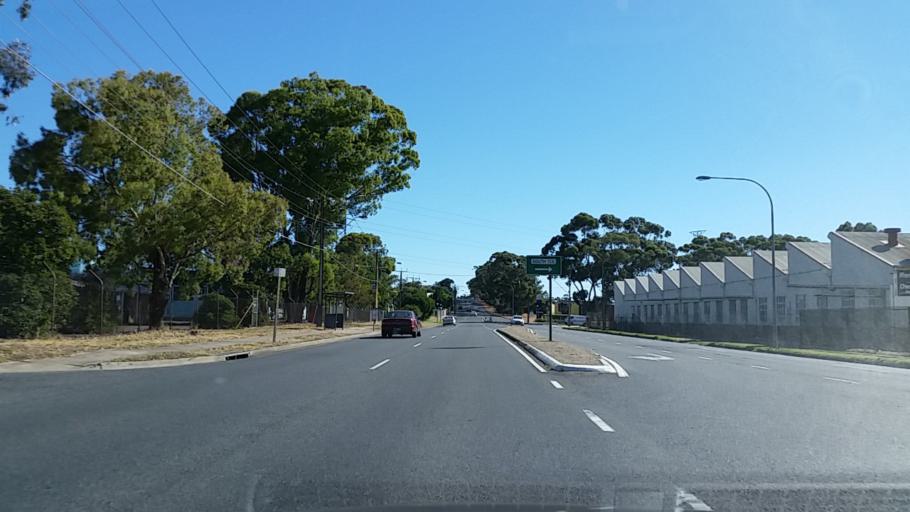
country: AU
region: South Australia
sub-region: Salisbury
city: Ingle Farm
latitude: -34.8369
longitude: 138.6249
